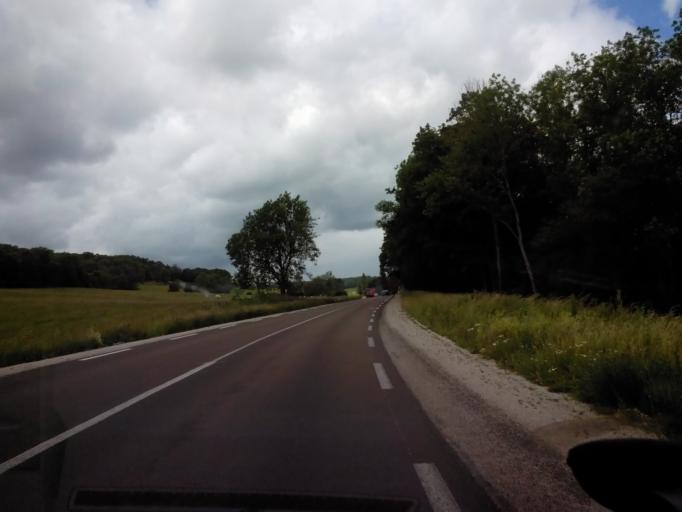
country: FR
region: Champagne-Ardenne
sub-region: Departement de la Haute-Marne
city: Rolampont
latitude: 47.9098
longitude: 5.2922
